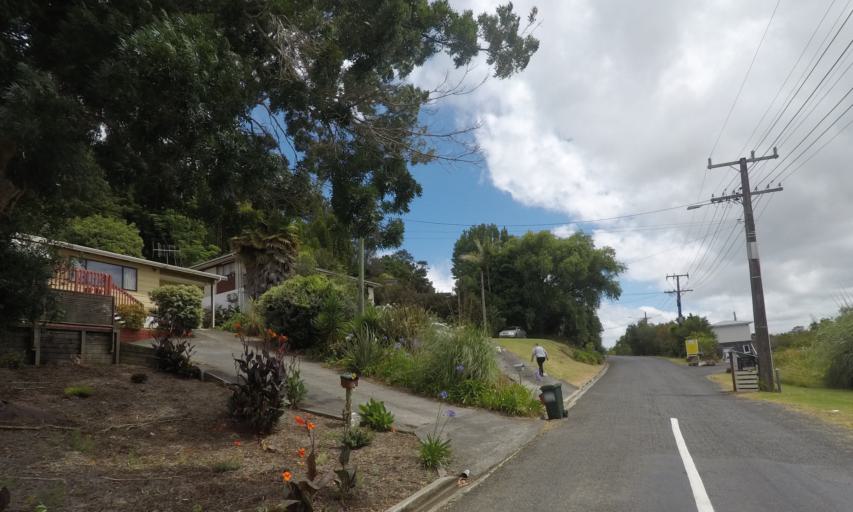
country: NZ
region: Northland
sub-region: Whangarei
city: Whangarei
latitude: -35.7423
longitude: 174.3619
